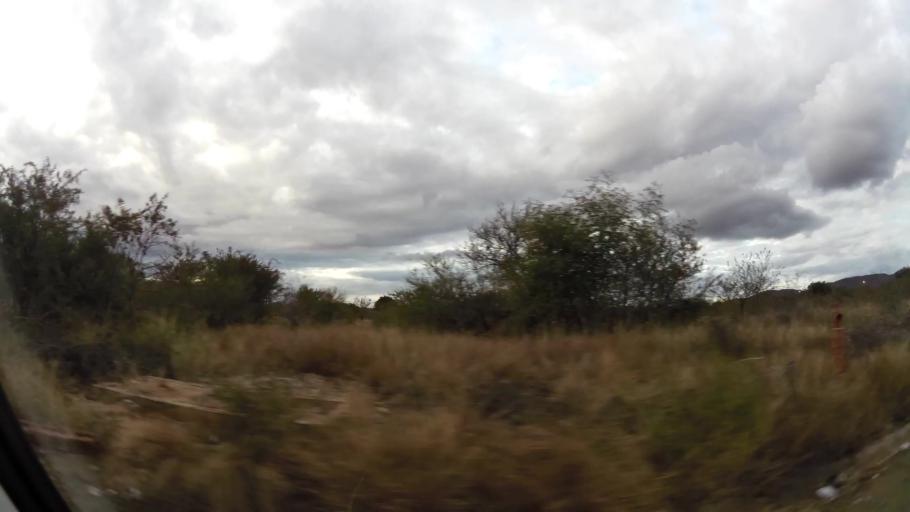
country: ZA
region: Limpopo
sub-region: Waterberg District Municipality
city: Mokopane
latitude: -24.1940
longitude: 28.9972
